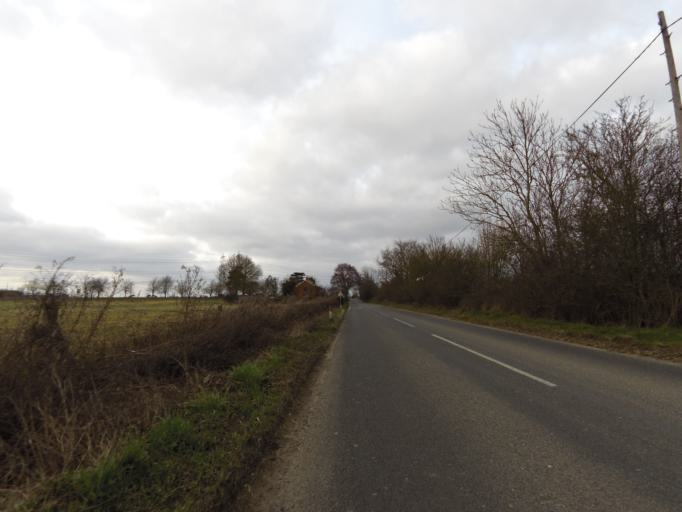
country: GB
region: England
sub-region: Suffolk
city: Ipswich
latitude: 52.0925
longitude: 1.1543
